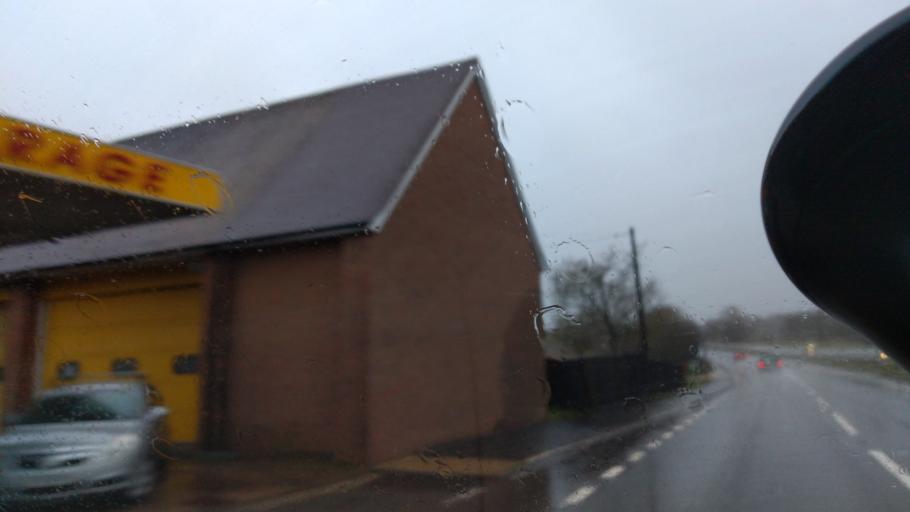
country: GB
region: England
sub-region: West Sussex
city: Rustington
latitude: 50.8407
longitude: -0.4858
